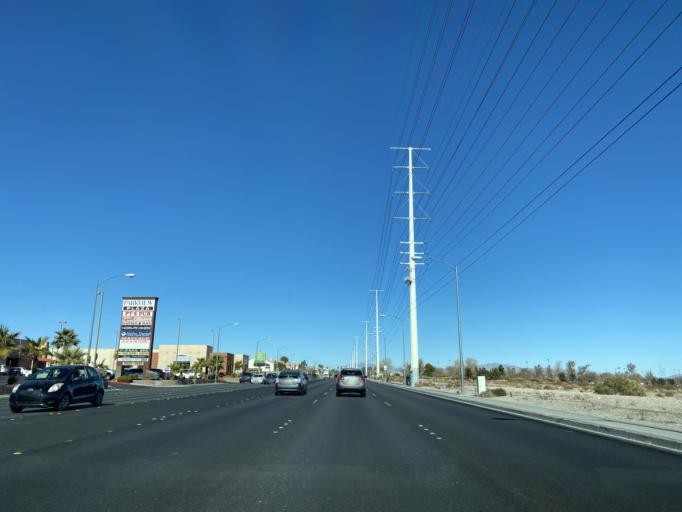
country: US
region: Nevada
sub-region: Clark County
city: Spring Valley
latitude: 36.1186
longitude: -115.2789
